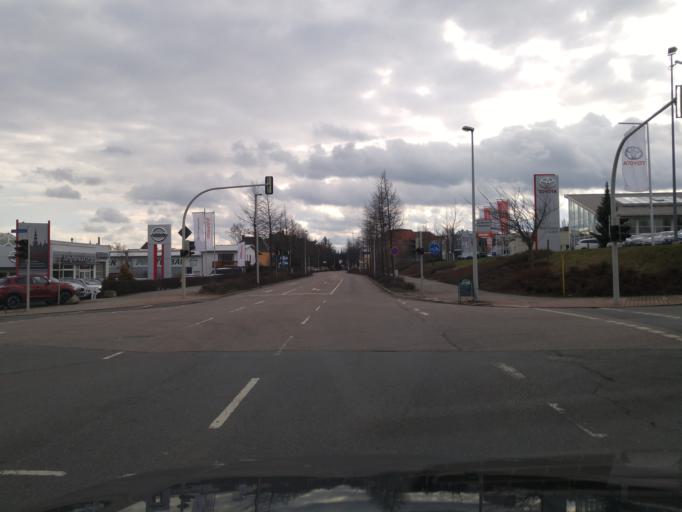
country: DE
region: Saxony
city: Weissenborn
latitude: 50.7271
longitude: 12.4743
